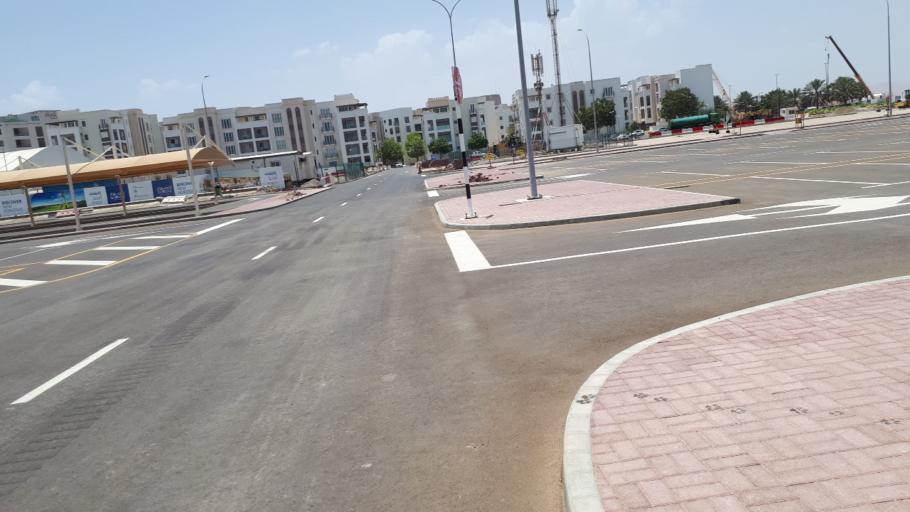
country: OM
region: Muhafazat Masqat
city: As Sib al Jadidah
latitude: 23.6318
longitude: 58.2651
